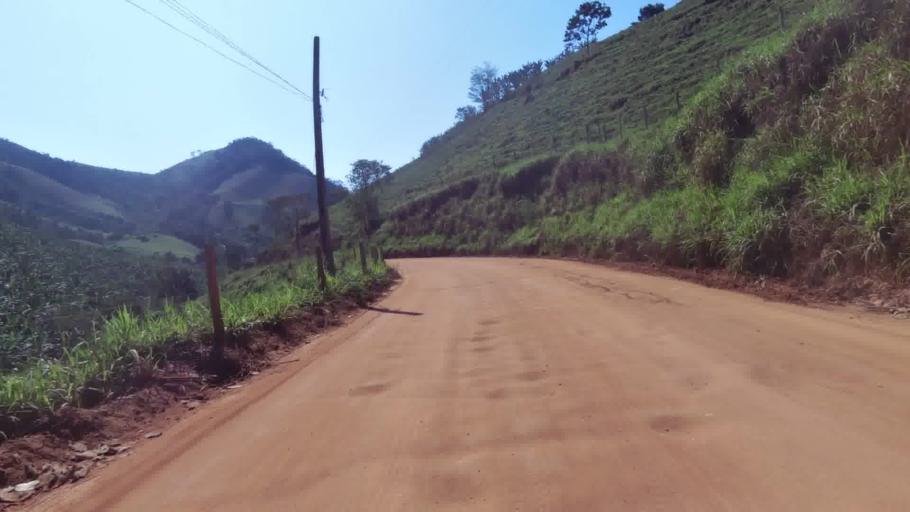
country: BR
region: Espirito Santo
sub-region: Alfredo Chaves
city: Alfredo Chaves
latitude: -20.6500
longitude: -40.8037
